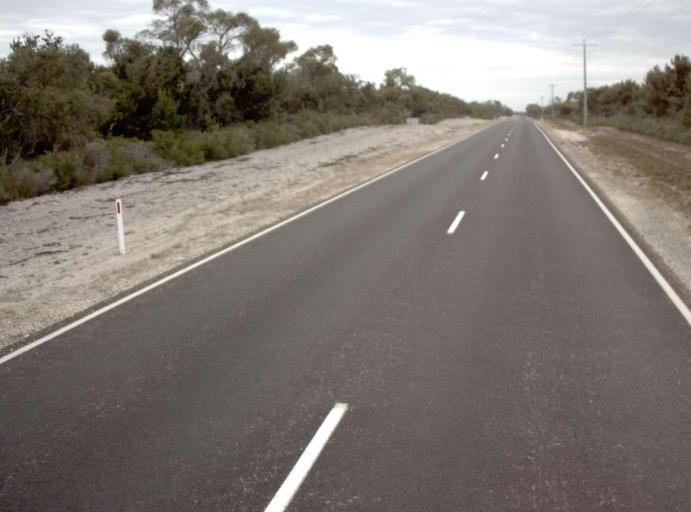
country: AU
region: Victoria
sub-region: Wellington
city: Sale
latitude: -38.1703
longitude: 147.3848
